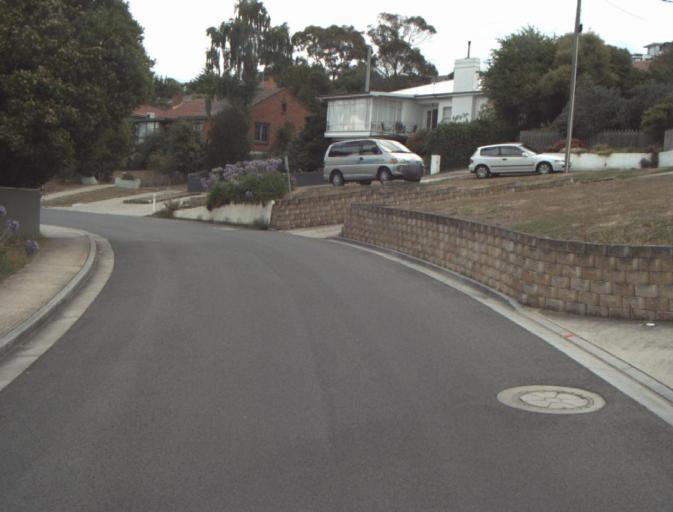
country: AU
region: Tasmania
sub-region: Launceston
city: Launceston
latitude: -41.4259
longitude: 147.1132
